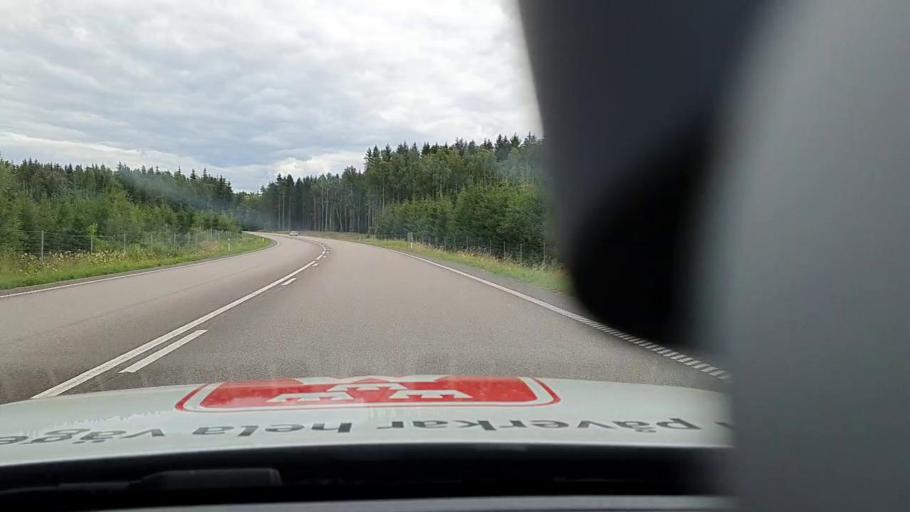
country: SE
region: Vaestra Goetaland
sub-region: Lidkopings Kommun
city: Vinninga
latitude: 58.4459
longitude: 13.2468
